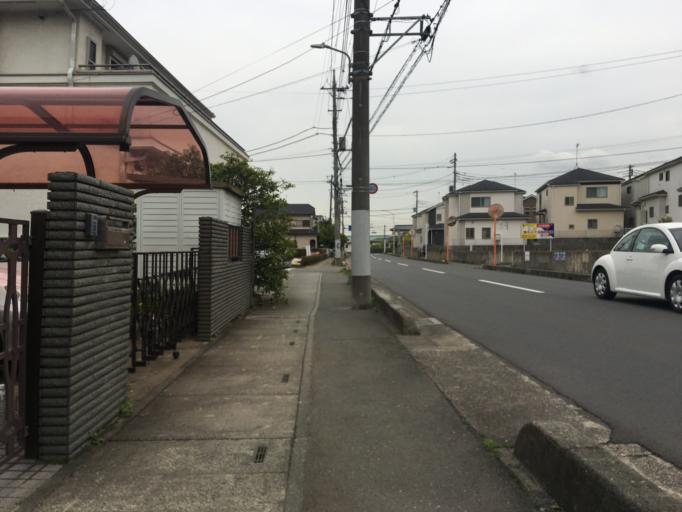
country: JP
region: Saitama
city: Oi
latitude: 35.8538
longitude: 139.5520
